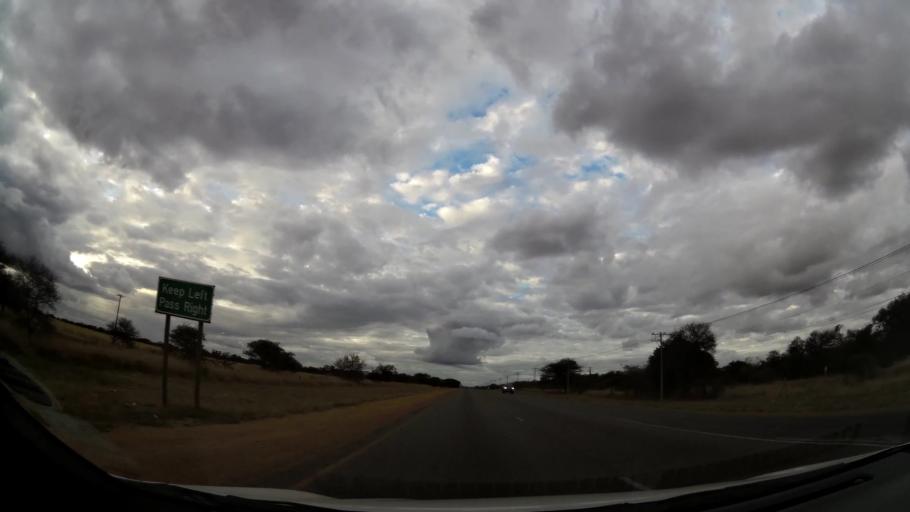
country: ZA
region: Limpopo
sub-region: Waterberg District Municipality
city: Mokopane
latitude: -24.2383
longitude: 28.9957
